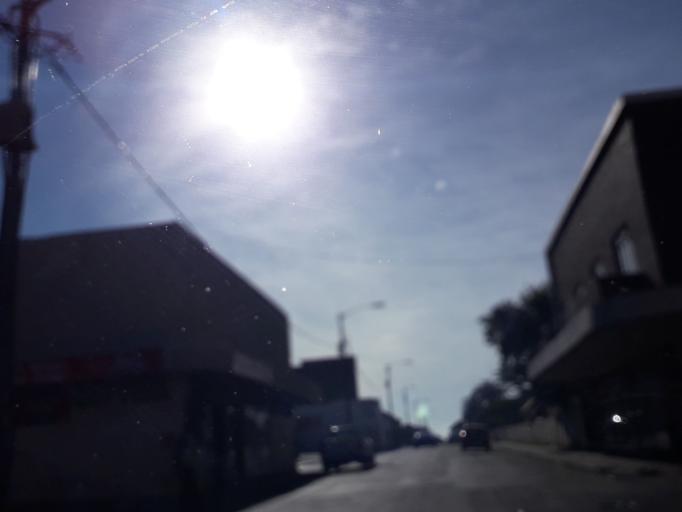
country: ZA
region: Gauteng
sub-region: City of Johannesburg Metropolitan Municipality
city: Johannesburg
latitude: -26.1925
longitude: 27.9983
